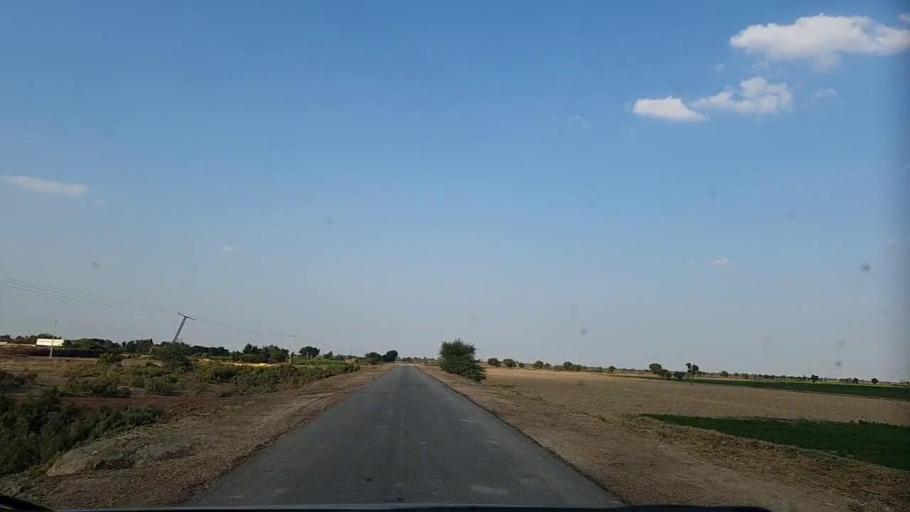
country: PK
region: Sindh
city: Pithoro
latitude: 25.6899
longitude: 69.2221
